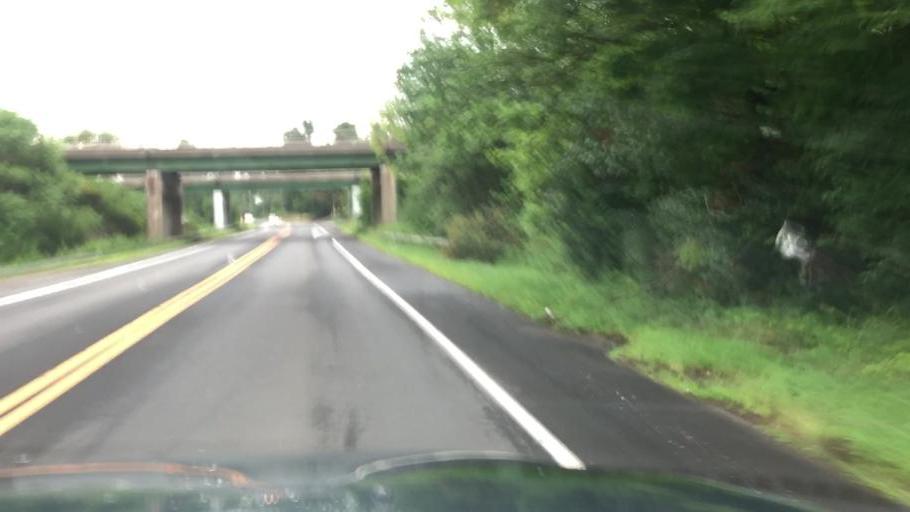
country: US
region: New York
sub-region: Dutchess County
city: Beacon
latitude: 41.5293
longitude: -73.9419
